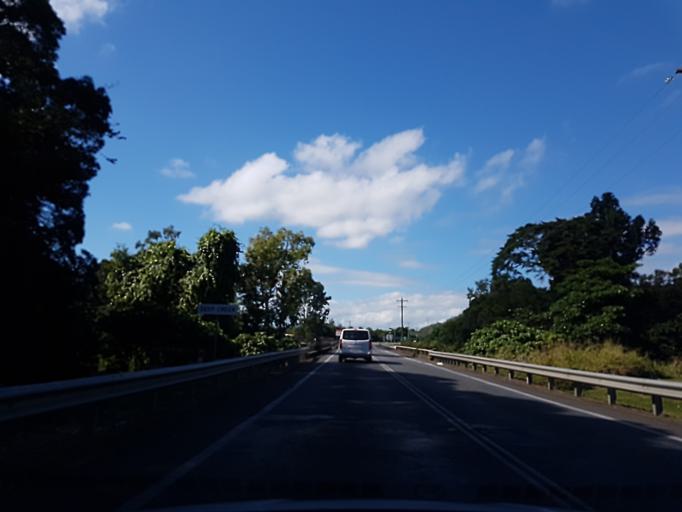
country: AU
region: Queensland
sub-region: Cairns
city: Trinity Beach
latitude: -16.7873
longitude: 145.6751
